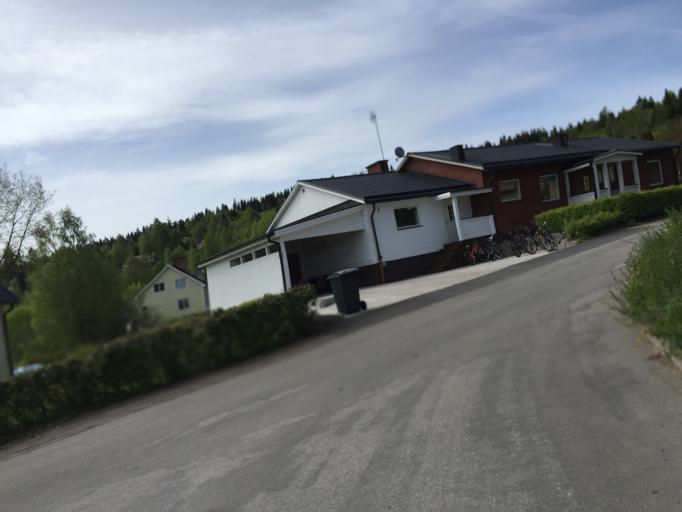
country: SE
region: Dalarna
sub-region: Ludvika Kommun
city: Ludvika
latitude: 60.1331
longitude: 15.1615
